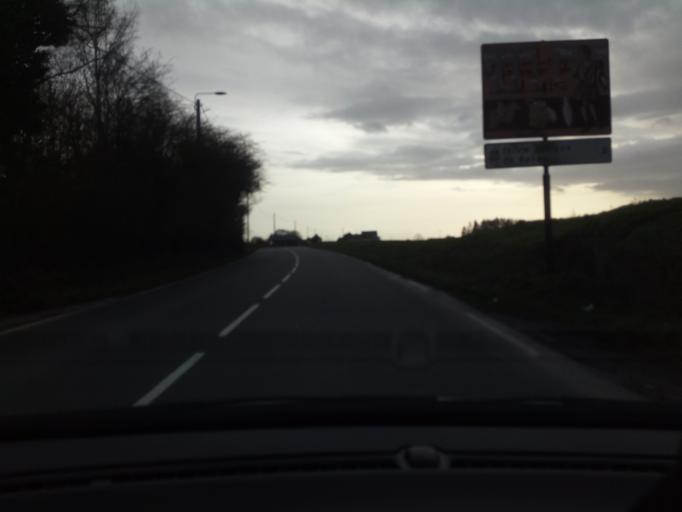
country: FR
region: Nord-Pas-de-Calais
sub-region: Departement du Nord
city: La Longueville
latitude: 50.3296
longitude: 3.8682
